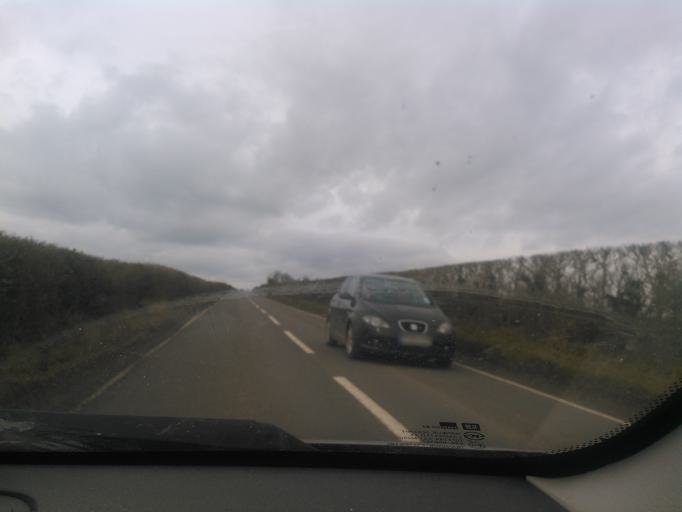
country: GB
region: England
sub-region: Shropshire
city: Wem
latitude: 52.8310
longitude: -2.6946
